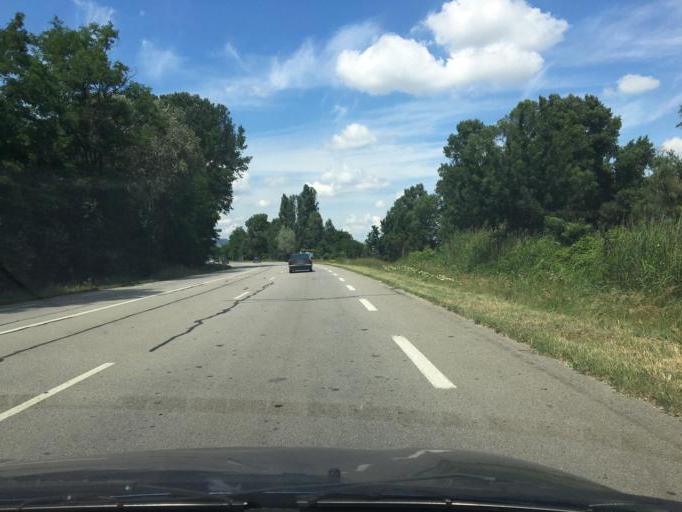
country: FR
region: Rhone-Alpes
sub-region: Departement de l'Ardeche
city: Charmes-sur-Rhone
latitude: 44.8512
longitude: 4.8528
